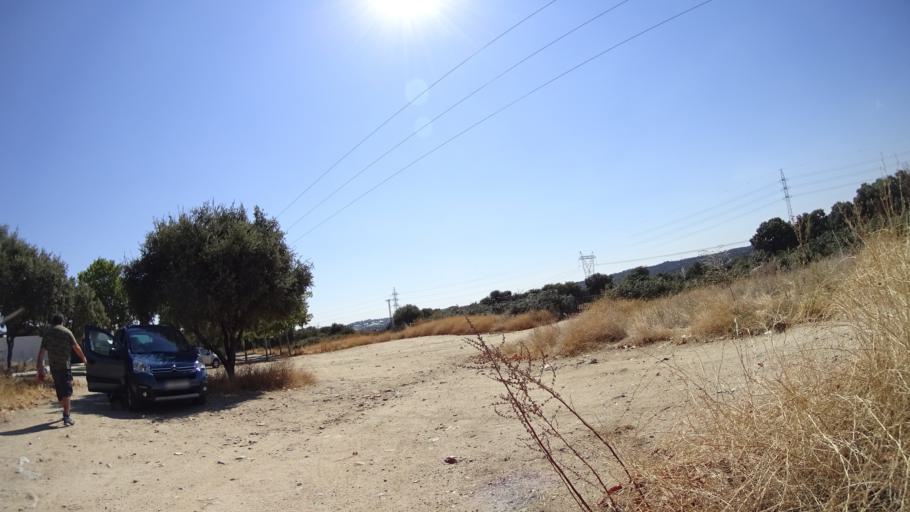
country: ES
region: Madrid
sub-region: Provincia de Madrid
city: Galapagar
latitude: 40.5988
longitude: -4.0114
